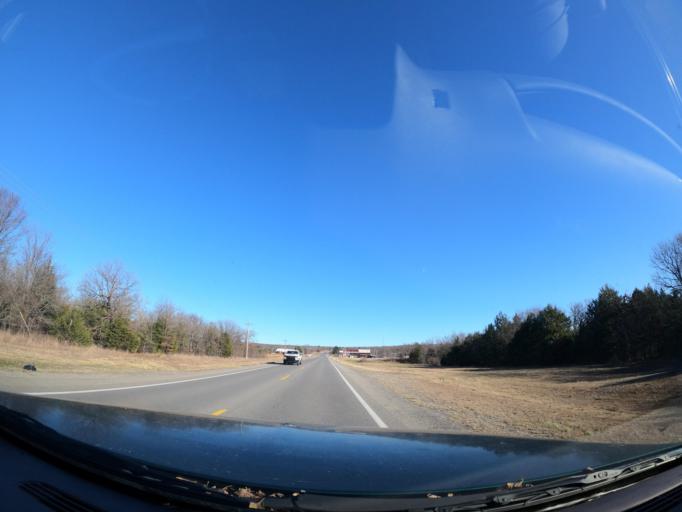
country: US
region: Oklahoma
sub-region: Pittsburg County
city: Longtown
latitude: 35.2392
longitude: -95.4833
